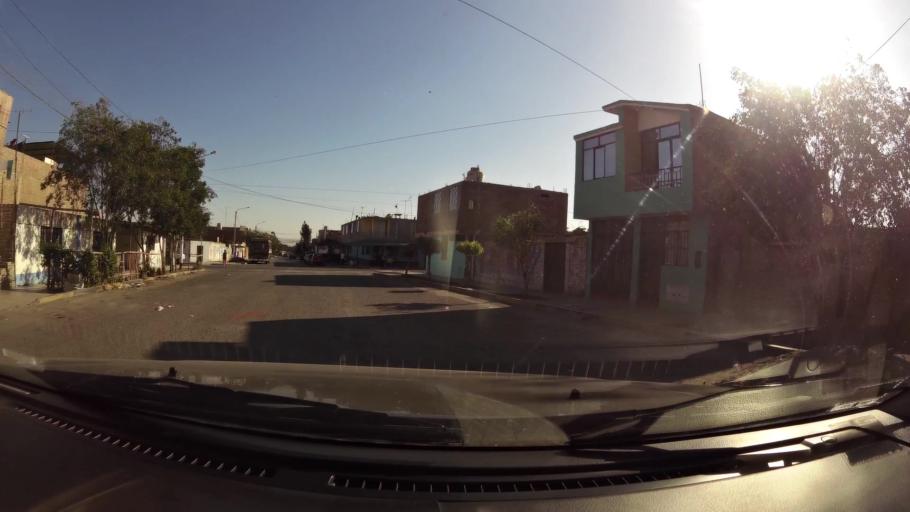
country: PE
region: Ica
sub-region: Provincia de Ica
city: La Tinguina
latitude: -14.0472
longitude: -75.6974
